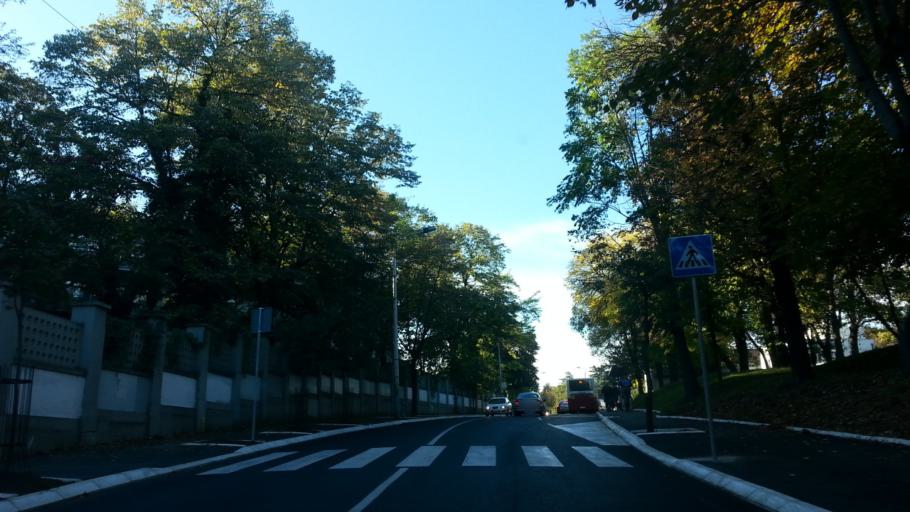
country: RS
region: Central Serbia
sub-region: Belgrade
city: Savski Venac
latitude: 44.7802
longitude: 20.4589
